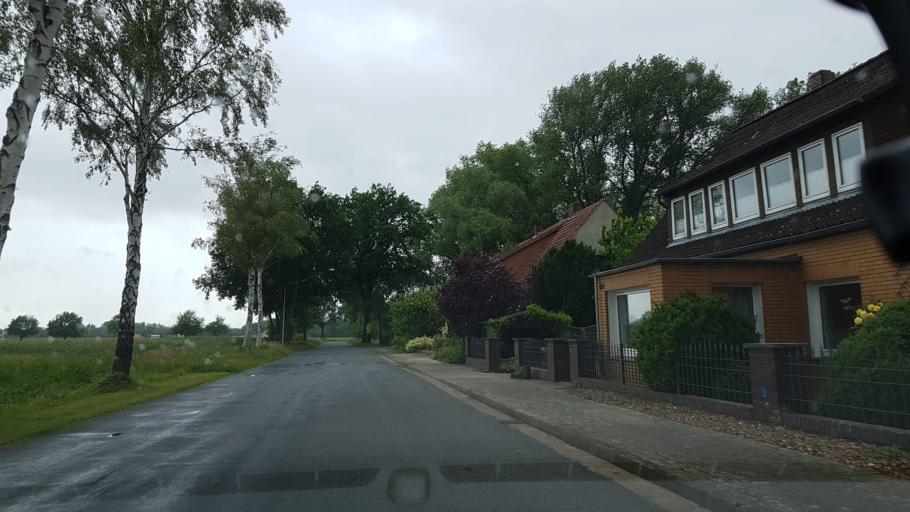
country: DE
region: Lower Saxony
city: Neustadt am Rubenberge
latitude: 52.5291
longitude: 9.5243
